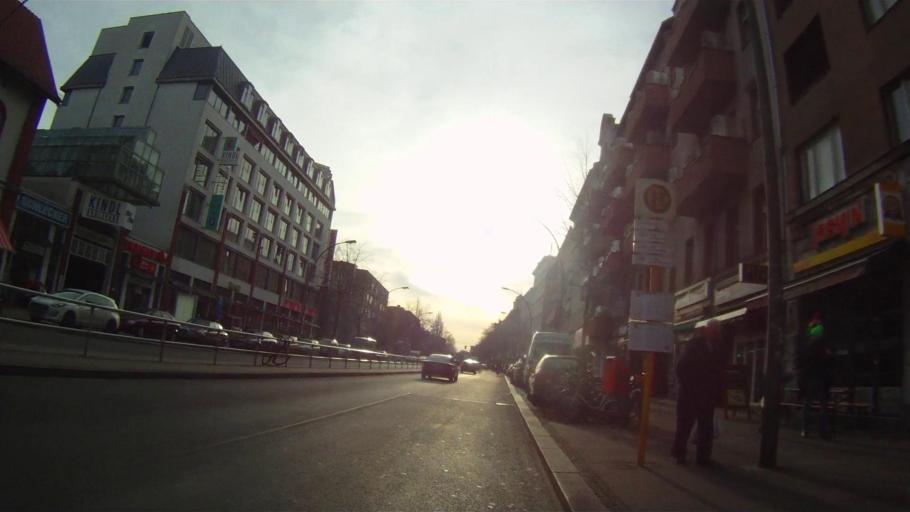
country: DE
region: Berlin
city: Berlin Treptow
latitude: 52.4790
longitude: 13.4255
